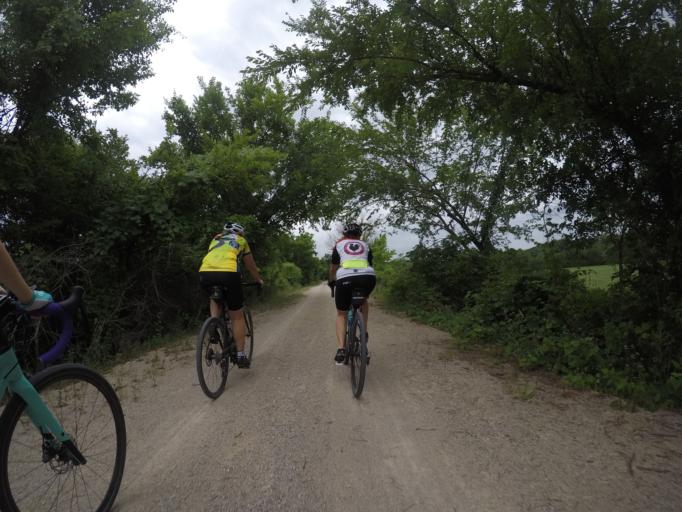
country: US
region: Kansas
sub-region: Anderson County
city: Garnett
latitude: 38.2504
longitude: -95.2533
